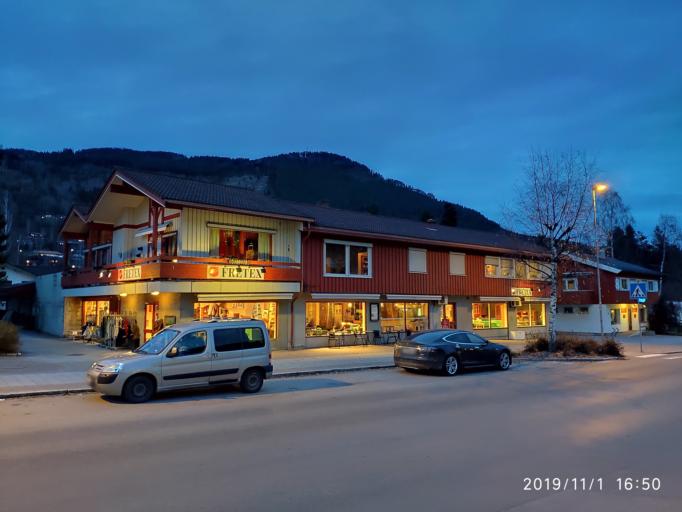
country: NO
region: Buskerud
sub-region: Gol
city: Gol
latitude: 60.7009
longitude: 8.9501
